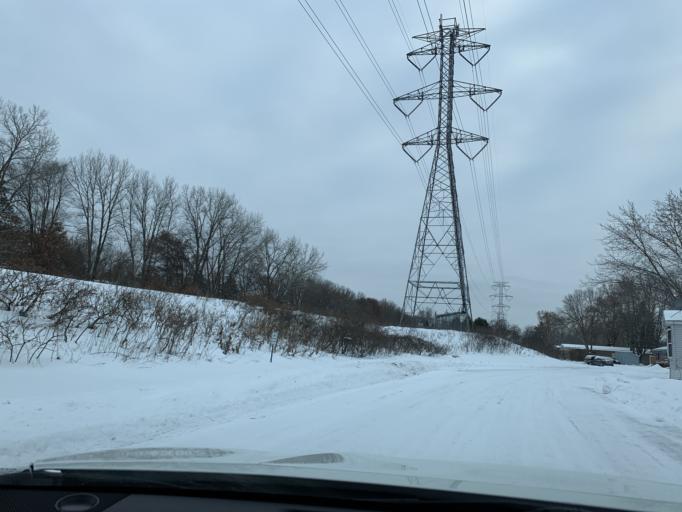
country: US
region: Minnesota
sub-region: Anoka County
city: Coon Rapids
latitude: 45.1585
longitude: -93.2945
